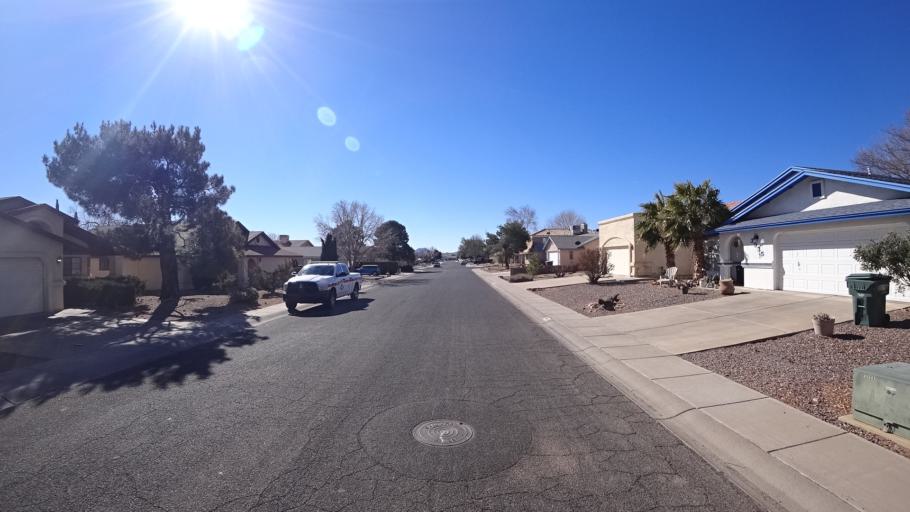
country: US
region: Arizona
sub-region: Mohave County
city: New Kingman-Butler
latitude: 35.2371
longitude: -114.0389
